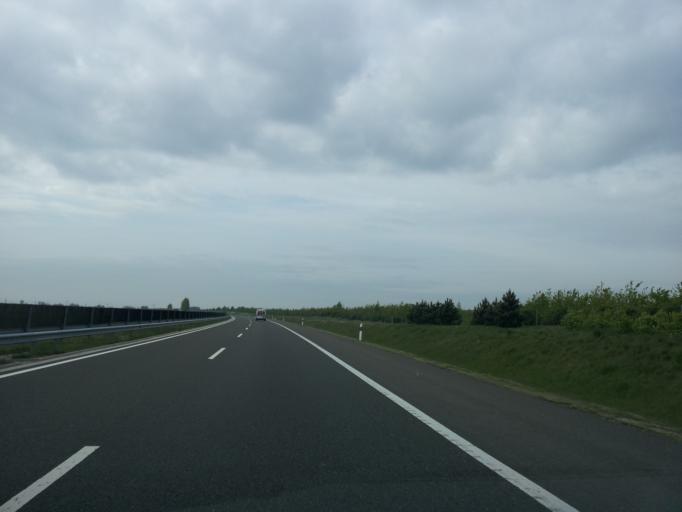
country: HU
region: Fejer
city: Baracs
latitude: 46.8900
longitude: 18.8759
